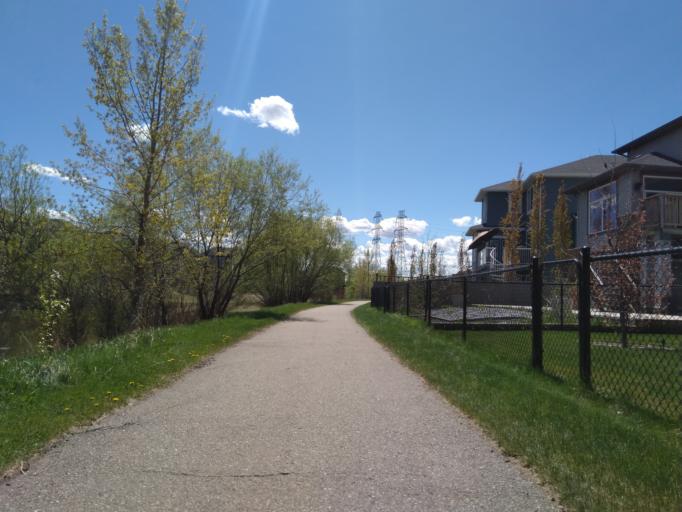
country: CA
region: Alberta
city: Chestermere
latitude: 51.0255
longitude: -113.8342
